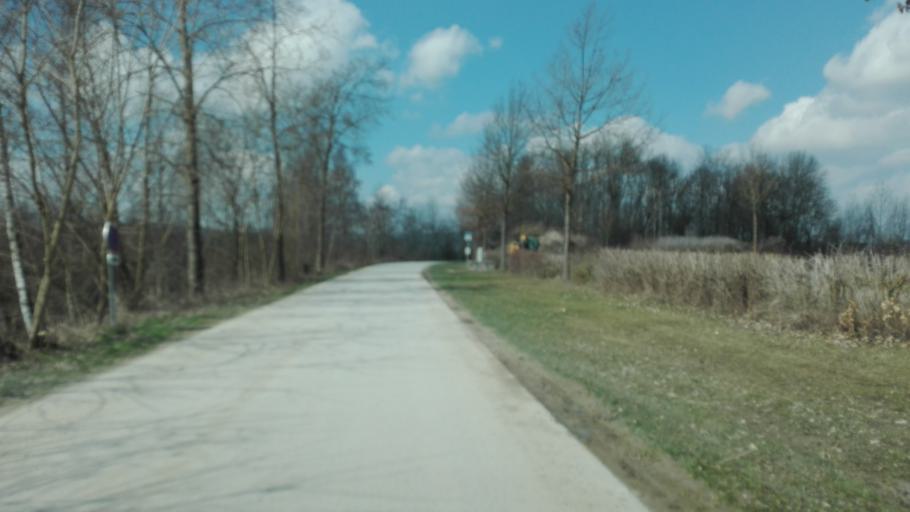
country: AT
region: Upper Austria
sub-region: Politischer Bezirk Urfahr-Umgebung
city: Feldkirchen an der Donau
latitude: 48.3214
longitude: 14.0675
